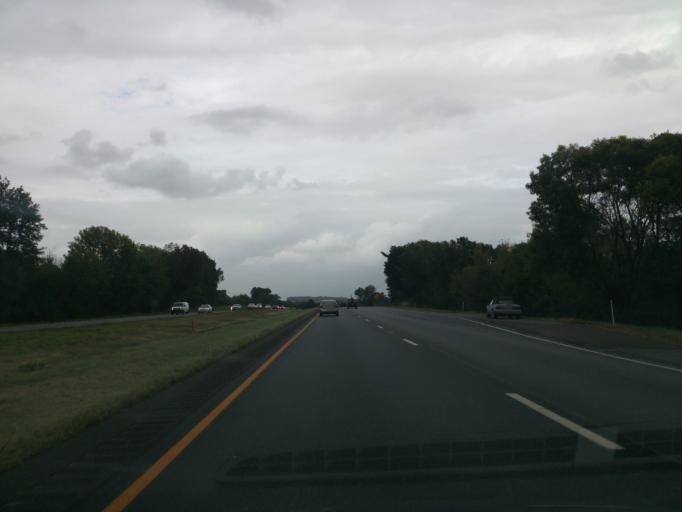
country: US
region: Pennsylvania
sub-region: Lancaster County
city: Brownstown
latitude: 40.0977
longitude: -76.2591
